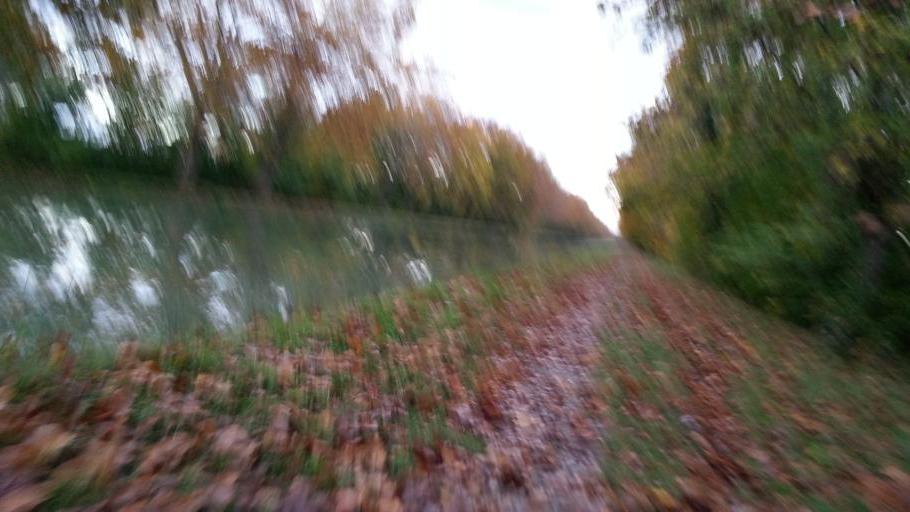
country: FR
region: Midi-Pyrenees
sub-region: Departement du Tarn-et-Garonne
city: Moissac
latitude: 44.0811
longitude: 1.1000
